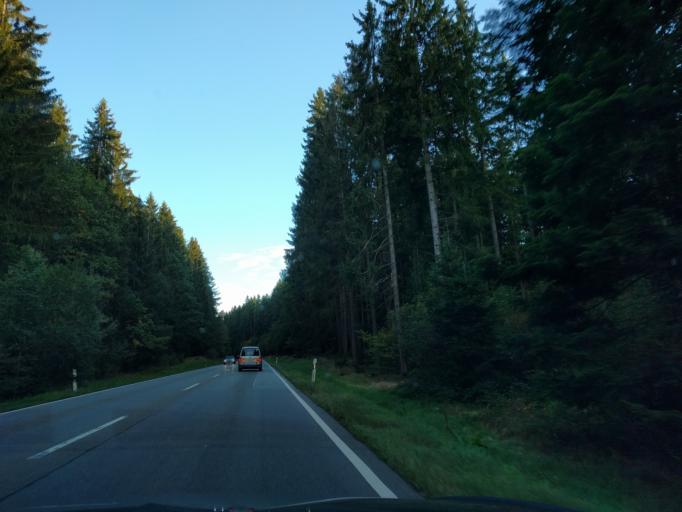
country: DE
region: Bavaria
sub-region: Lower Bavaria
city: Viechtach
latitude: 49.0498
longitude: 12.9254
